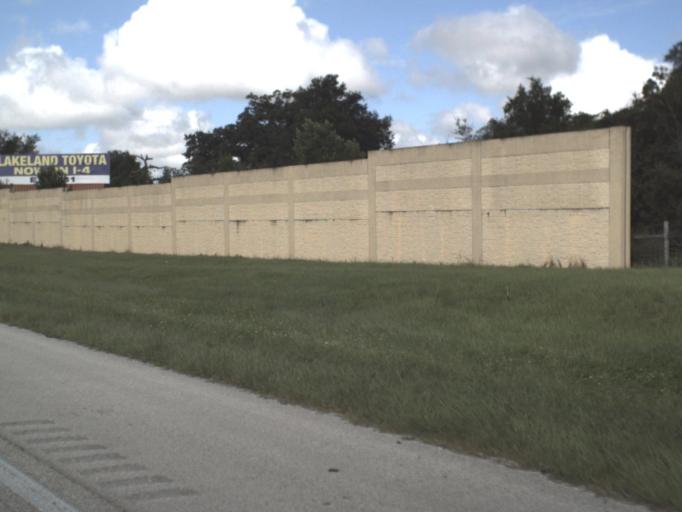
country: US
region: Florida
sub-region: Polk County
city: Gibsonia
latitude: 28.1227
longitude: -81.9291
